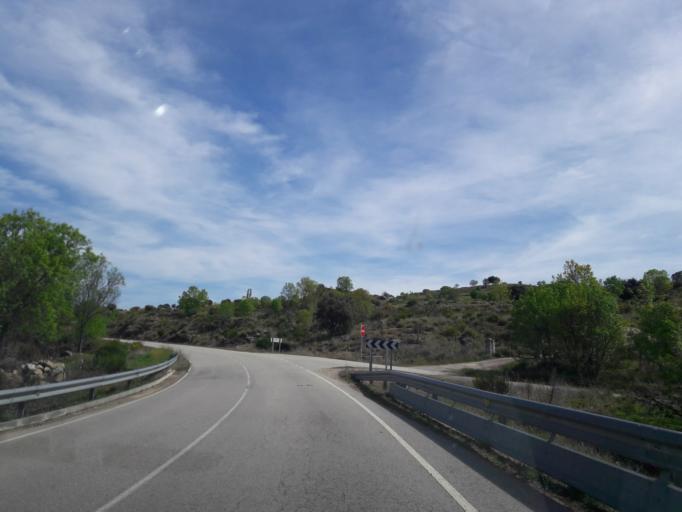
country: ES
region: Castille and Leon
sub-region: Provincia de Salamanca
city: Sanchotello
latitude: 40.4438
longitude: -5.7364
